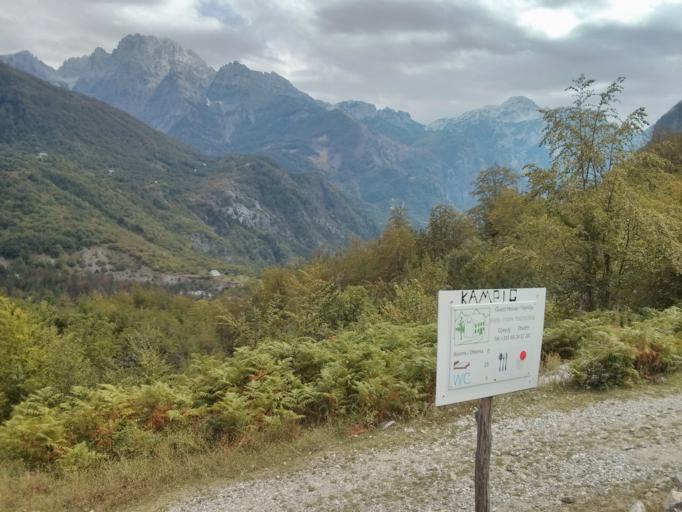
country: AL
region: Shkoder
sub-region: Rrethi i Shkodres
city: Nicaj-Shale
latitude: 42.4020
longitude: 19.7643
